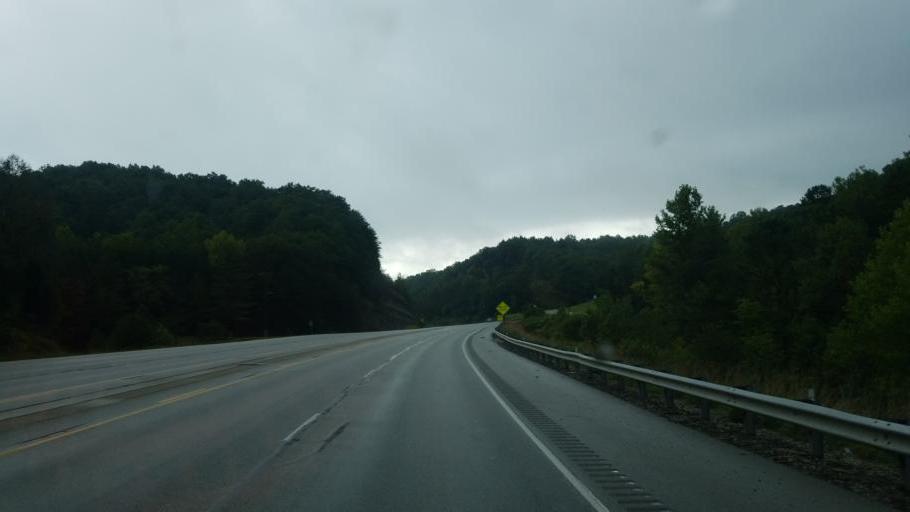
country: US
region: Kentucky
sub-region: Rowan County
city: Morehead
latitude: 38.1835
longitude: -83.4704
